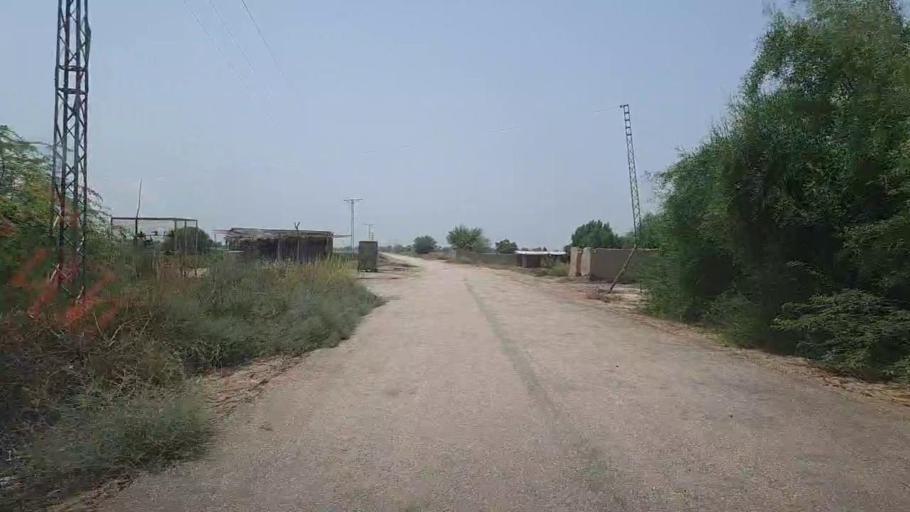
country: PK
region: Sindh
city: Pad Idan
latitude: 26.8342
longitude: 68.3232
